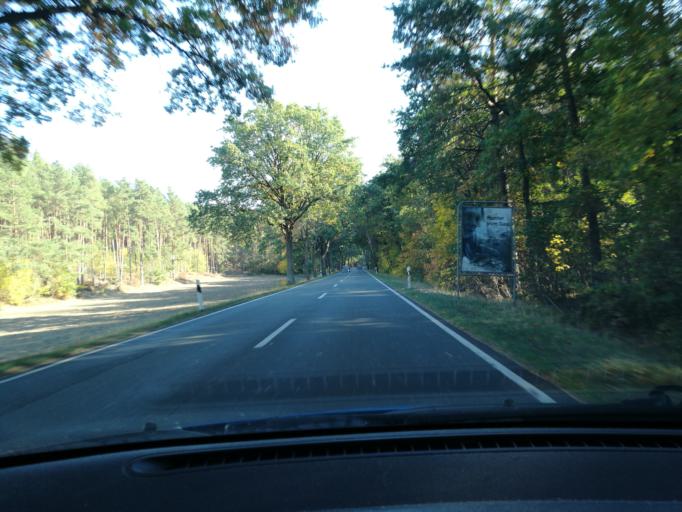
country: DE
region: Lower Saxony
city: Karwitz
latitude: 53.1266
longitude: 10.9762
